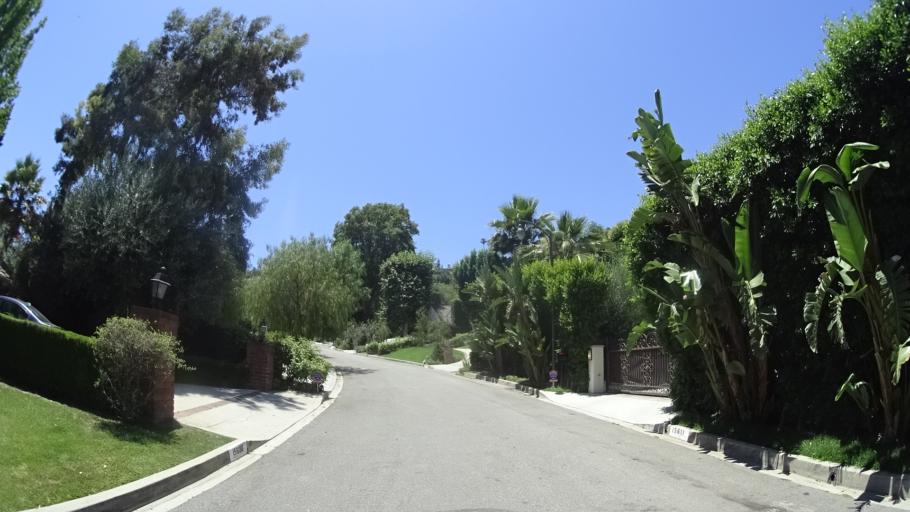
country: US
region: California
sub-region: Los Angeles County
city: Sherman Oaks
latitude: 34.1449
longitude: -118.4738
